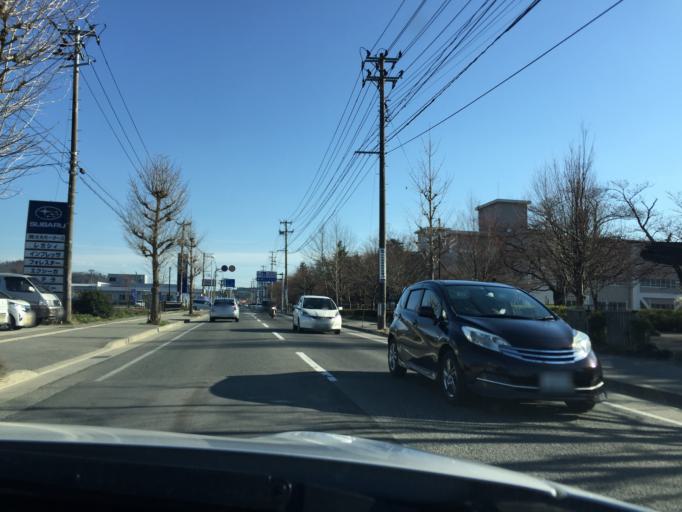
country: JP
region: Yamagata
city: Nagai
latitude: 38.1094
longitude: 140.0431
